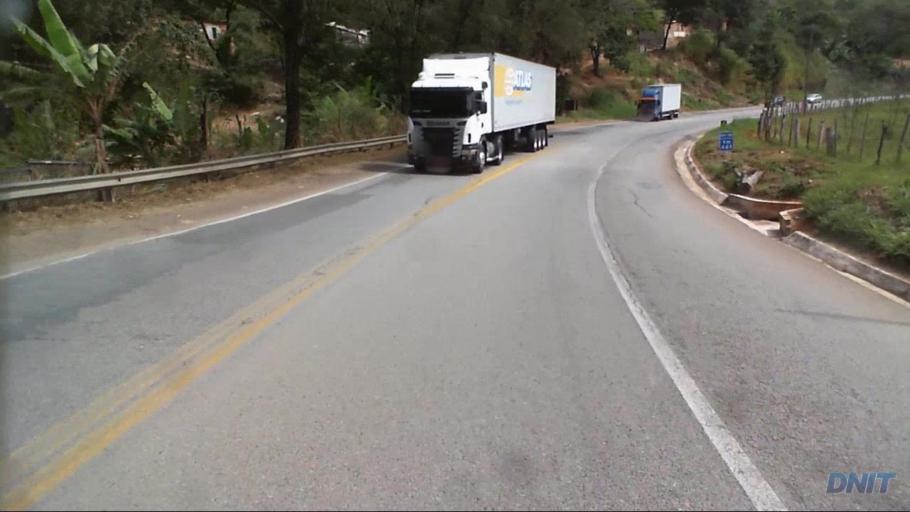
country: BR
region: Minas Gerais
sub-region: Santa Luzia
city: Santa Luzia
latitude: -19.8246
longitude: -43.8194
